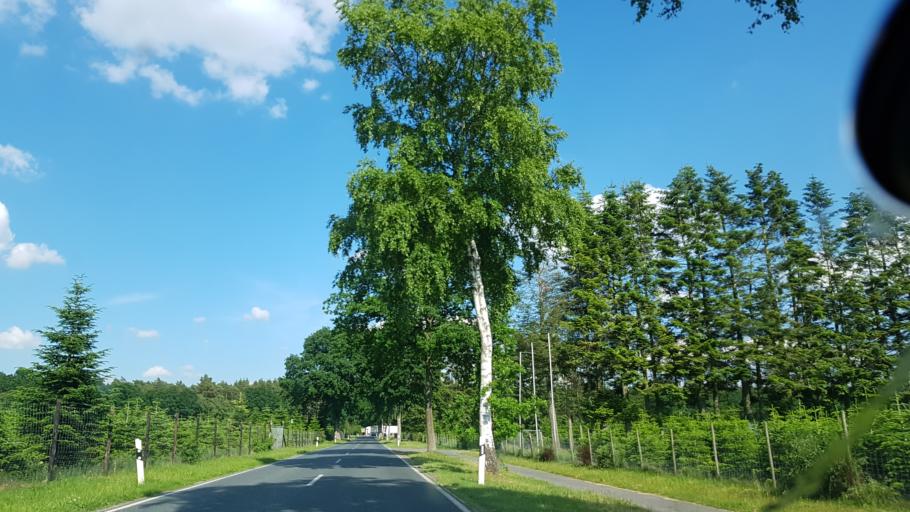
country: DE
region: Lower Saxony
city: Wenzendorf
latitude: 53.3461
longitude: 9.8052
